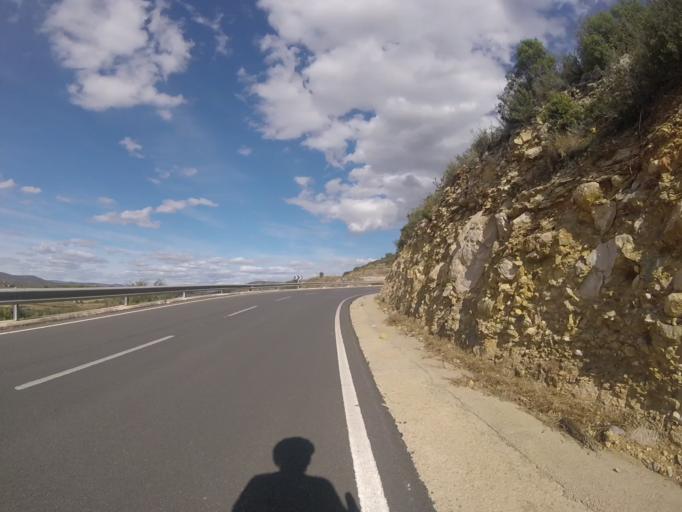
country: ES
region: Valencia
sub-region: Provincia de Castello
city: Cuevas de Vinroma
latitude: 40.3169
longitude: 0.1296
